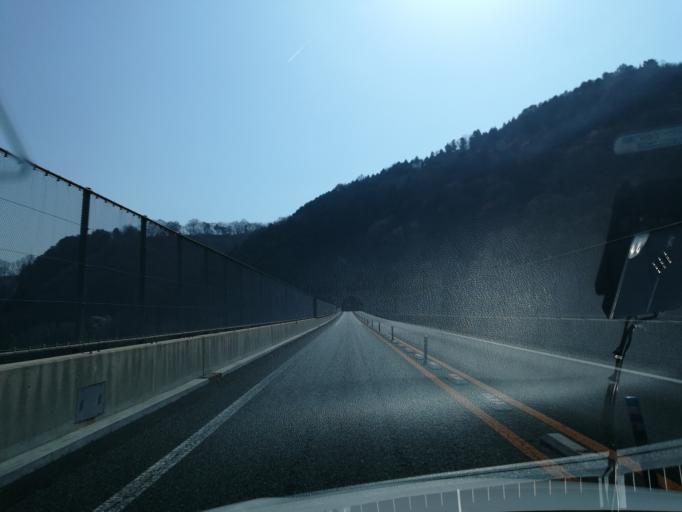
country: JP
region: Tokushima
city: Ikedacho
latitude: 34.0244
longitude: 133.7865
